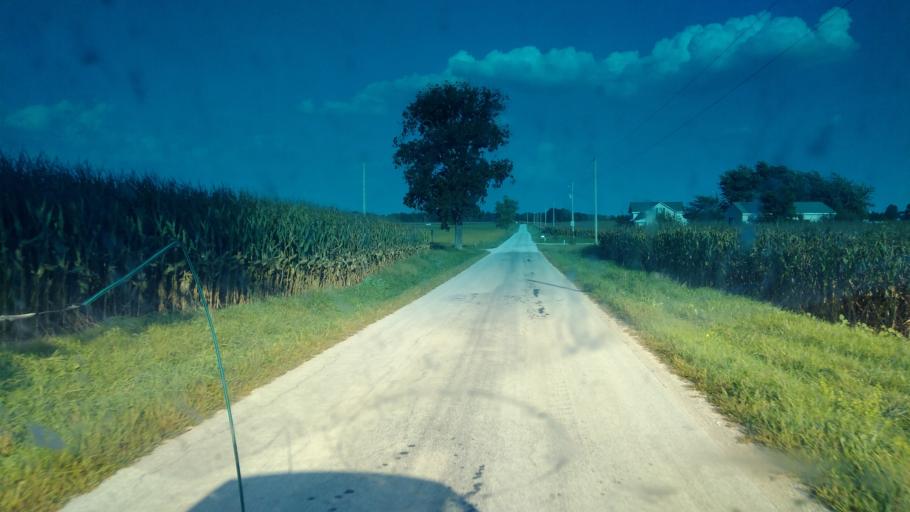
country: US
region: Ohio
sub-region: Wyandot County
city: Upper Sandusky
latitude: 40.9354
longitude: -83.1397
